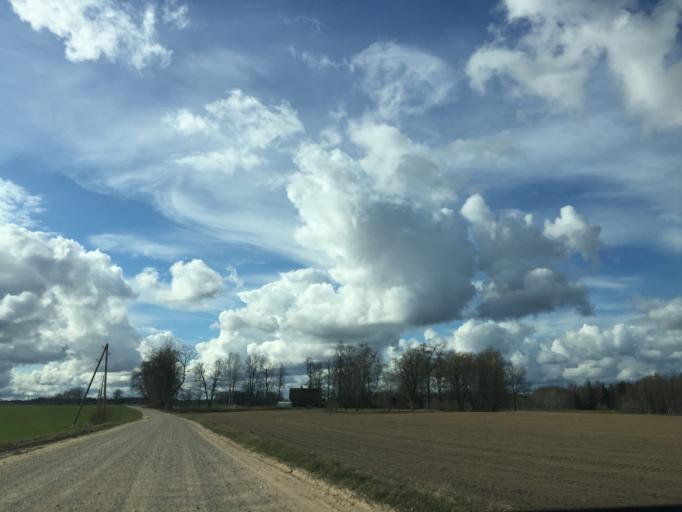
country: LV
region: Burtnieki
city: Matisi
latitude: 57.6094
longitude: 25.0378
